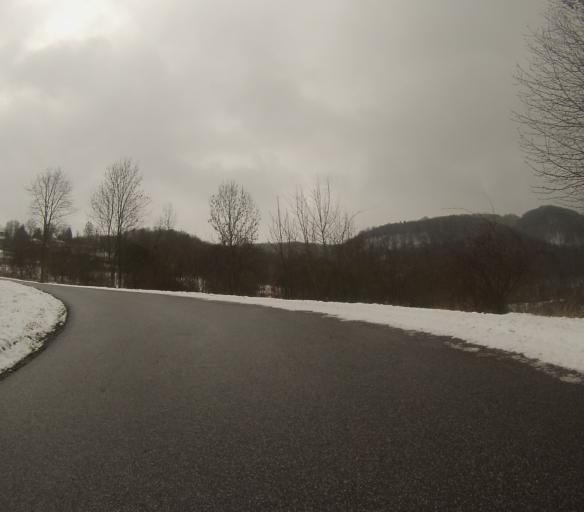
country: CZ
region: Ustecky
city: Benesov nad Ploucnici
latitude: 50.7421
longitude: 14.2667
